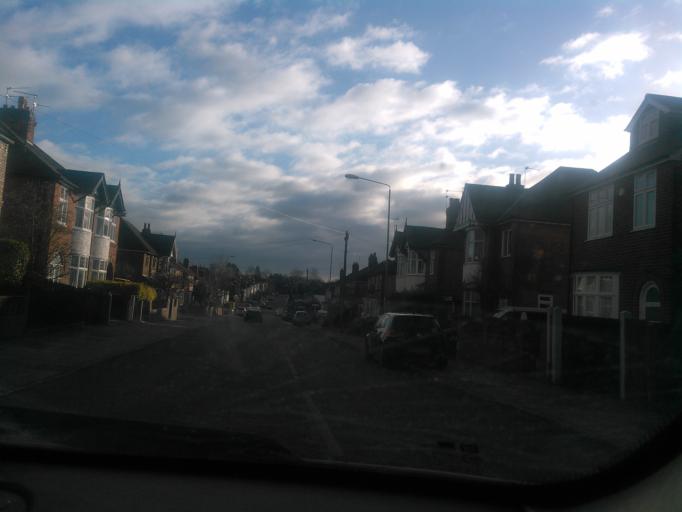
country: GB
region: England
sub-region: City of Leicester
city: Leicester
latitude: 52.6139
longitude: -1.1159
